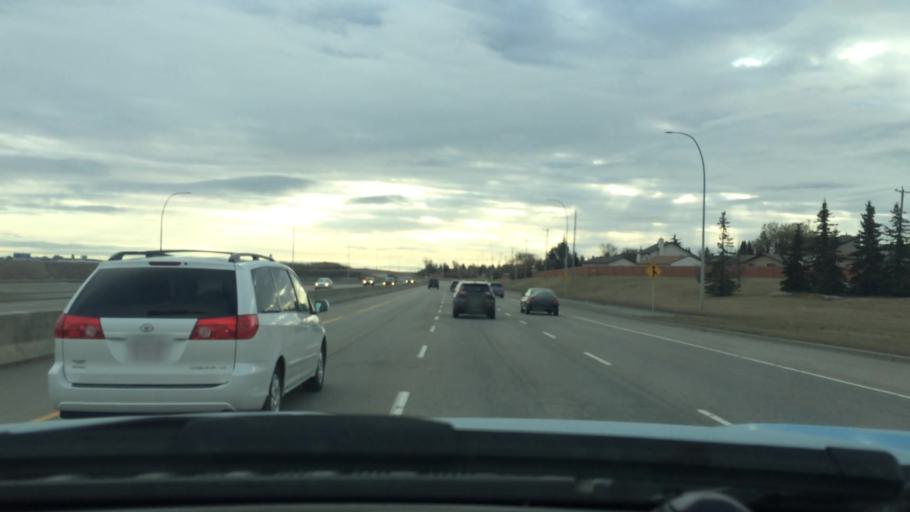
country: CA
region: Alberta
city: Calgary
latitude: 51.1333
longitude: -114.0691
